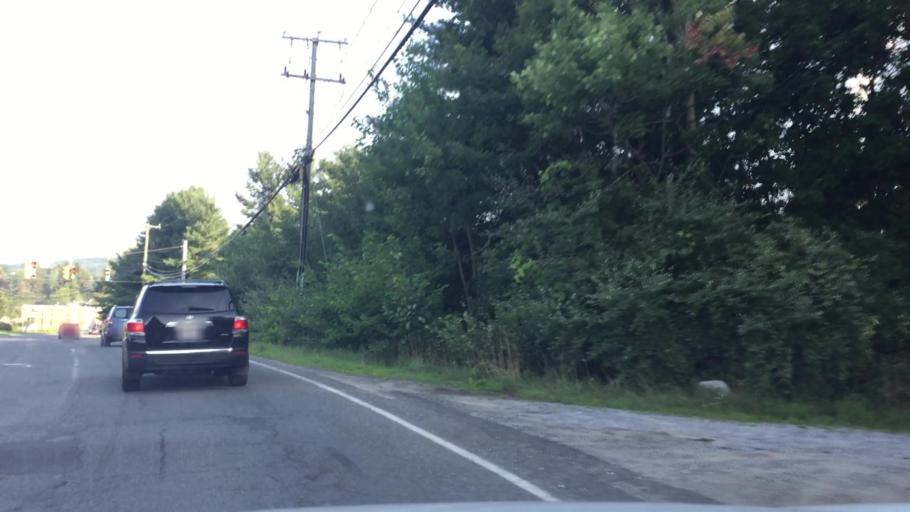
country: US
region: Massachusetts
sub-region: Berkshire County
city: Dalton
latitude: 42.4672
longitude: -73.1940
